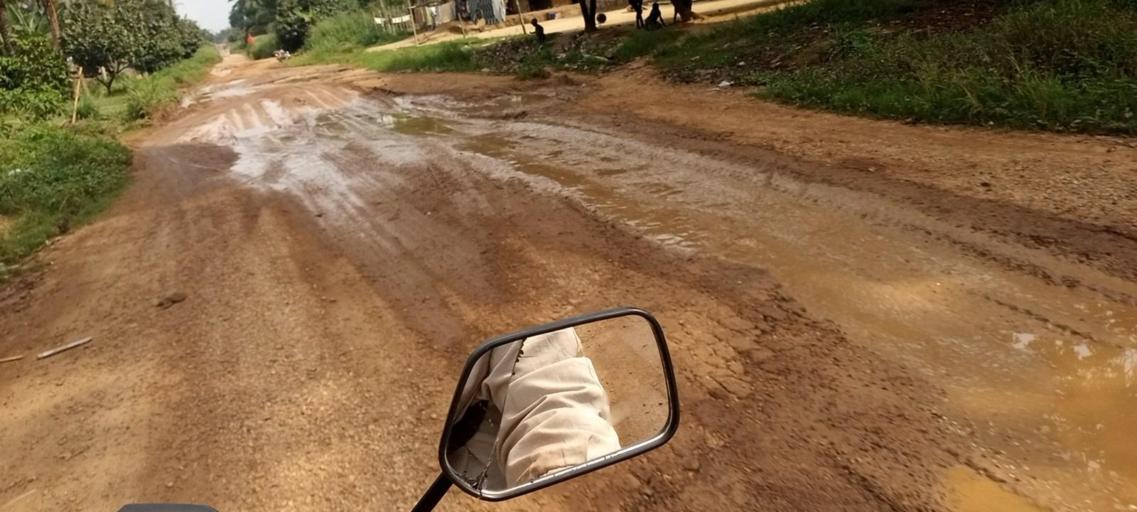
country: CD
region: Eastern Province
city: Kisangani
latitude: 0.4116
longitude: 25.3837
